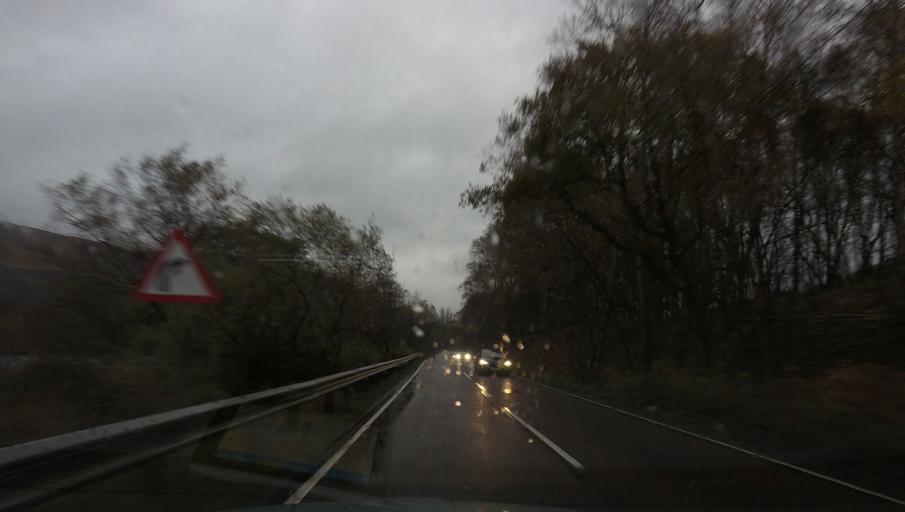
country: GB
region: Scotland
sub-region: Stirling
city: Callander
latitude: 56.4048
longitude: -4.5571
